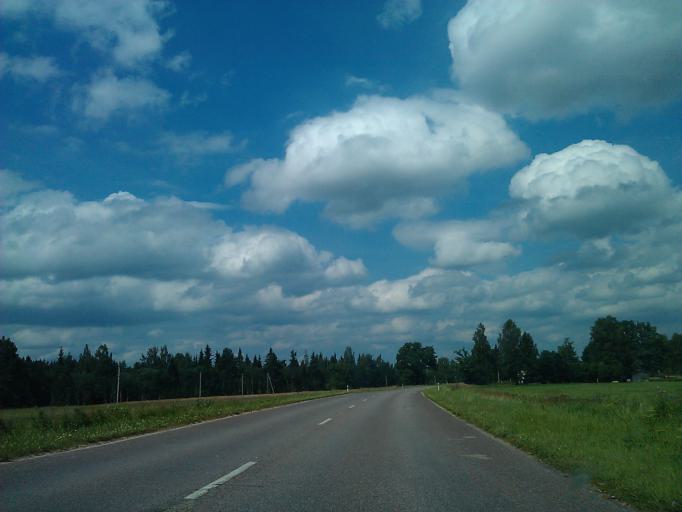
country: LV
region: Mazsalaca
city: Mazsalaca
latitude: 57.8377
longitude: 25.0595
